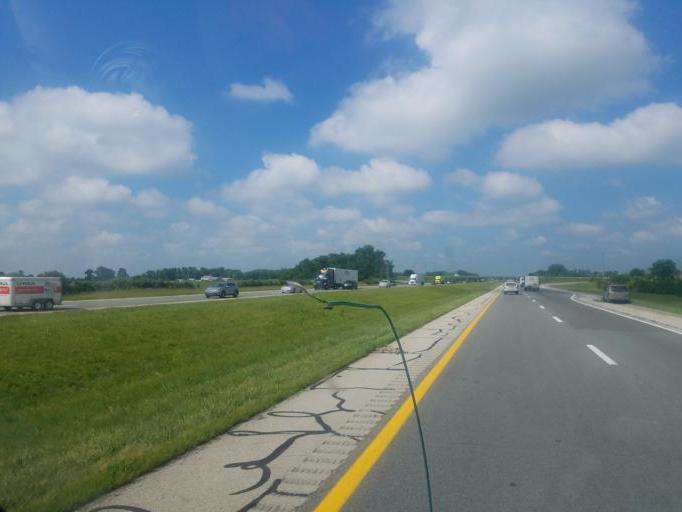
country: US
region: Ohio
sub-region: Madison County
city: Bethel
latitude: 39.6990
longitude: -83.4512
